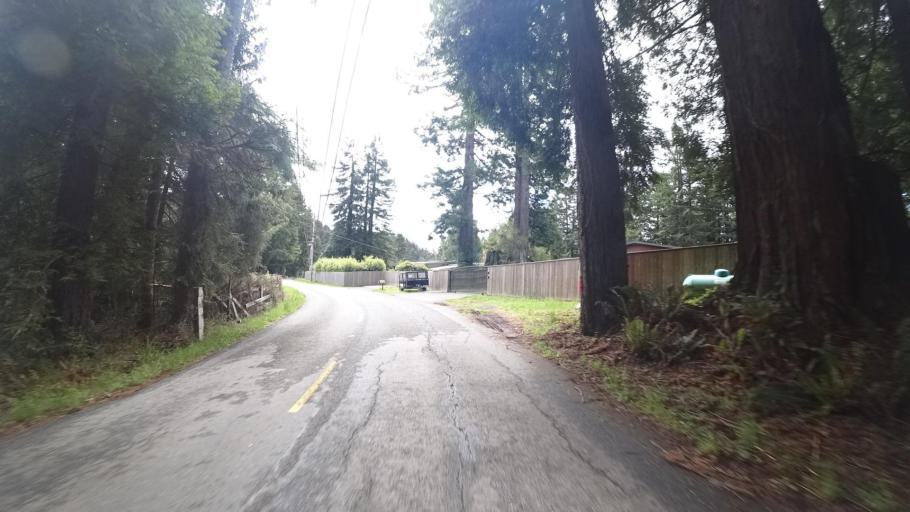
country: US
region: California
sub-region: Humboldt County
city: Bayside
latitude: 40.8636
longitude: -124.0427
